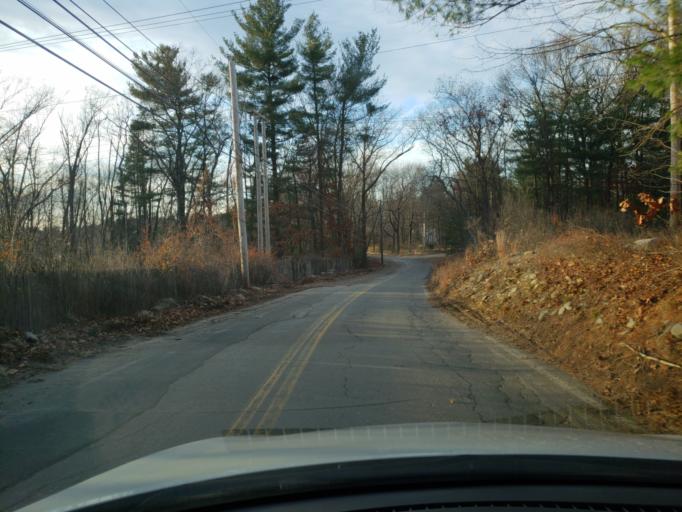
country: US
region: Massachusetts
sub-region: Essex County
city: Lawrence
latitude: 42.6738
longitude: -71.1916
